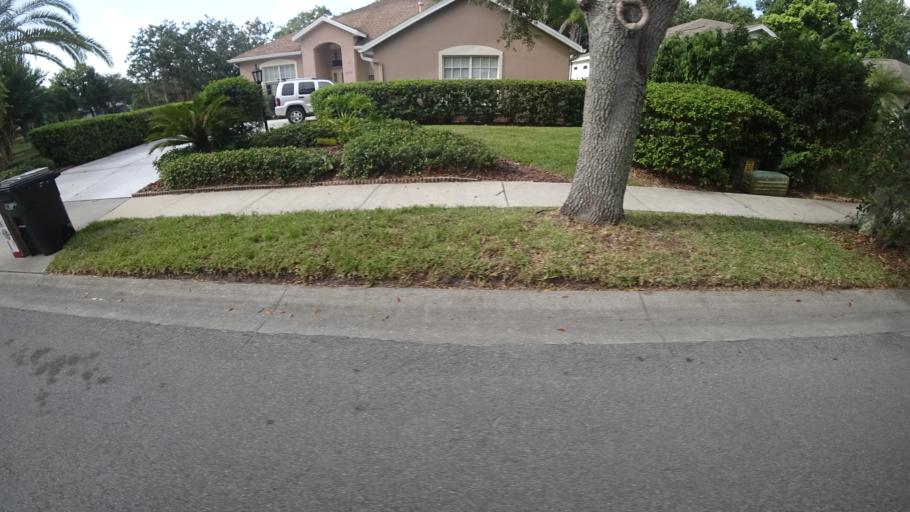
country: US
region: Florida
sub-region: Sarasota County
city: The Meadows
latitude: 27.4239
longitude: -82.4294
